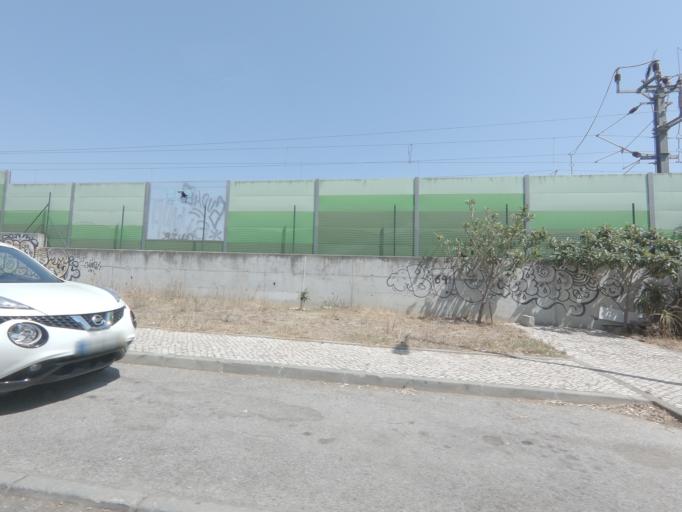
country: PT
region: Setubal
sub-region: Setubal
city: Setubal
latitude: 38.5419
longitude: -8.8828
